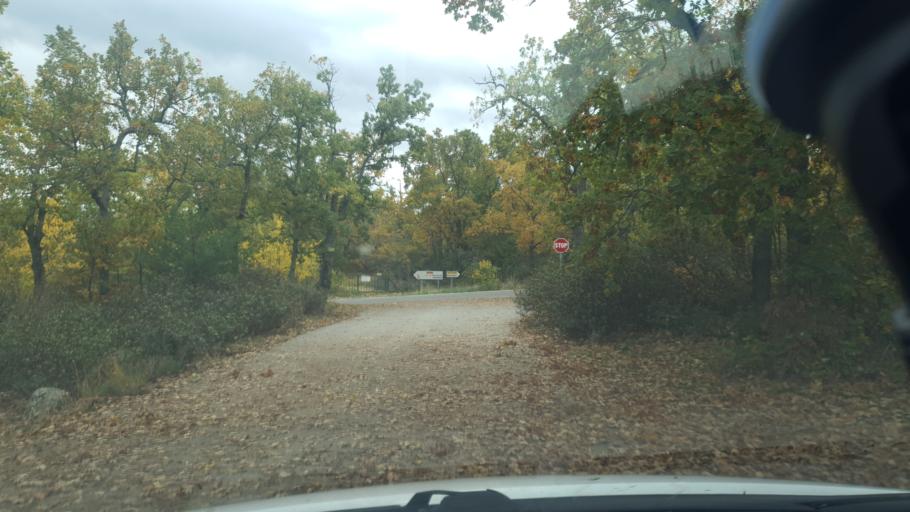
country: ES
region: Castille and Leon
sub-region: Provincia de Segovia
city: San Ildefonso
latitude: 40.9045
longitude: -4.0352
